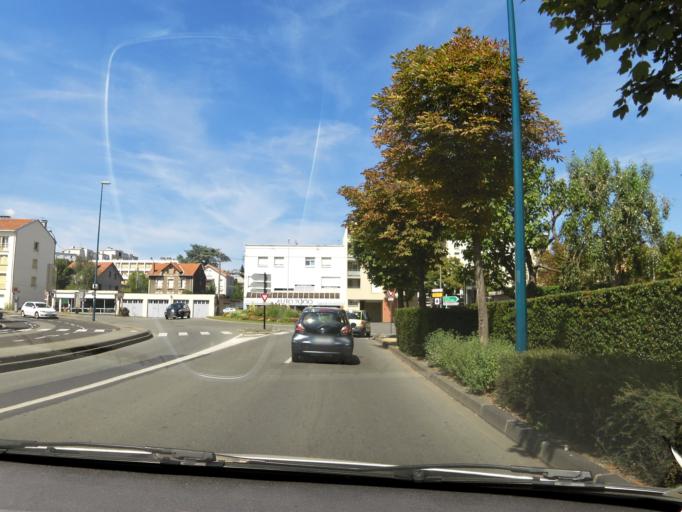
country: FR
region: Auvergne
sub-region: Departement du Puy-de-Dome
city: Chamalieres
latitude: 45.7810
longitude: 3.0709
